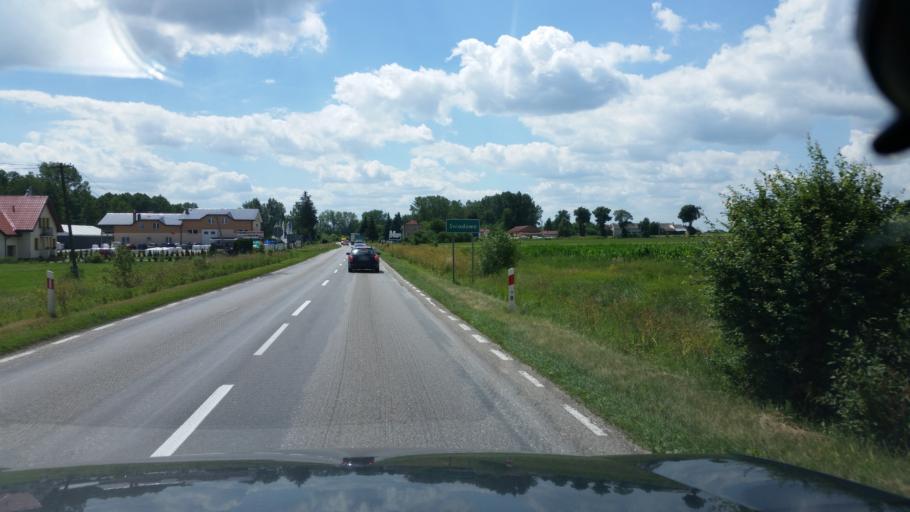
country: PL
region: Podlasie
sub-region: Powiat lomzynski
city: Sniadowo
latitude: 53.0497
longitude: 21.9935
